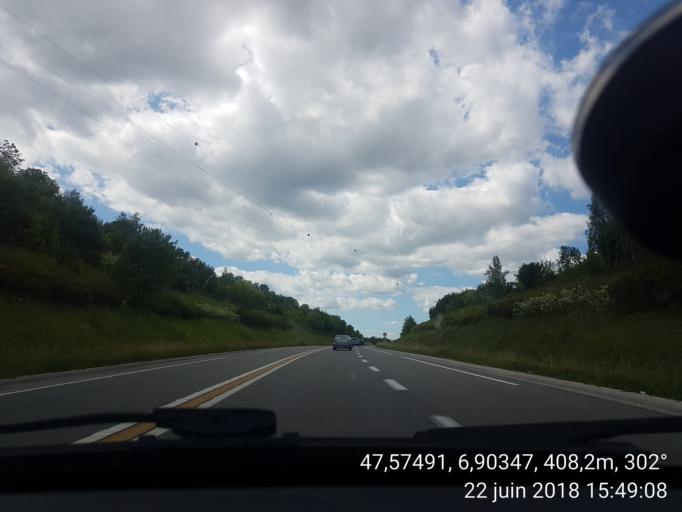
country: FR
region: Franche-Comte
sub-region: Territoire de Belfort
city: Bourogne
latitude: 47.5750
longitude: 6.9034
